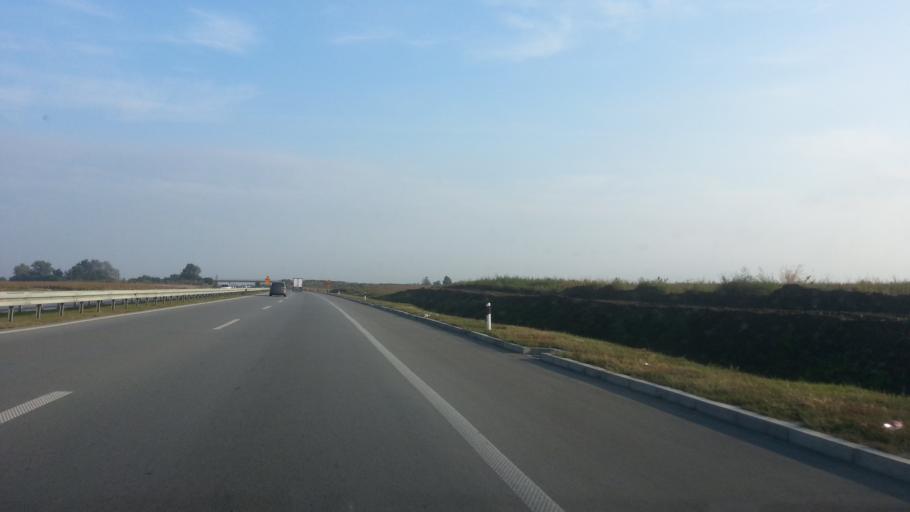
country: RS
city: Novi Banovci
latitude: 44.9105
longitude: 20.3055
